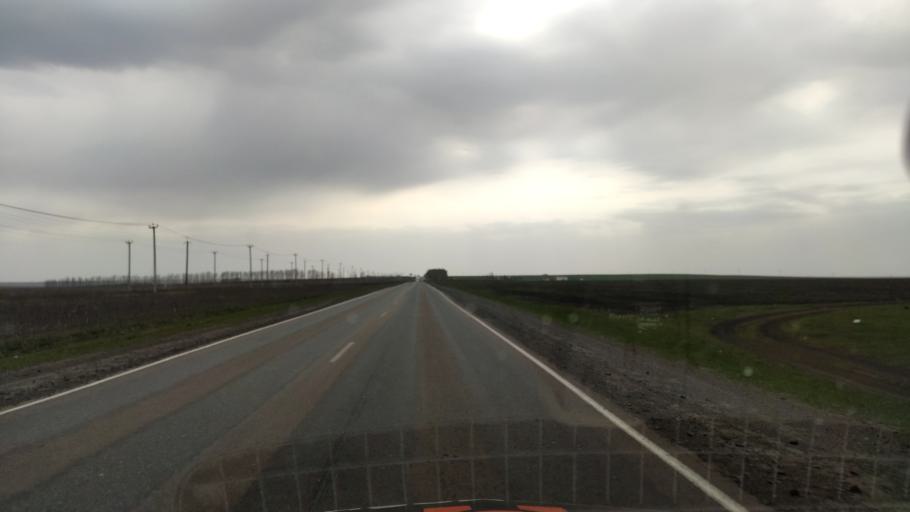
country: RU
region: Kursk
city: Gorshechnoye
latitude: 51.5141
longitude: 38.0083
